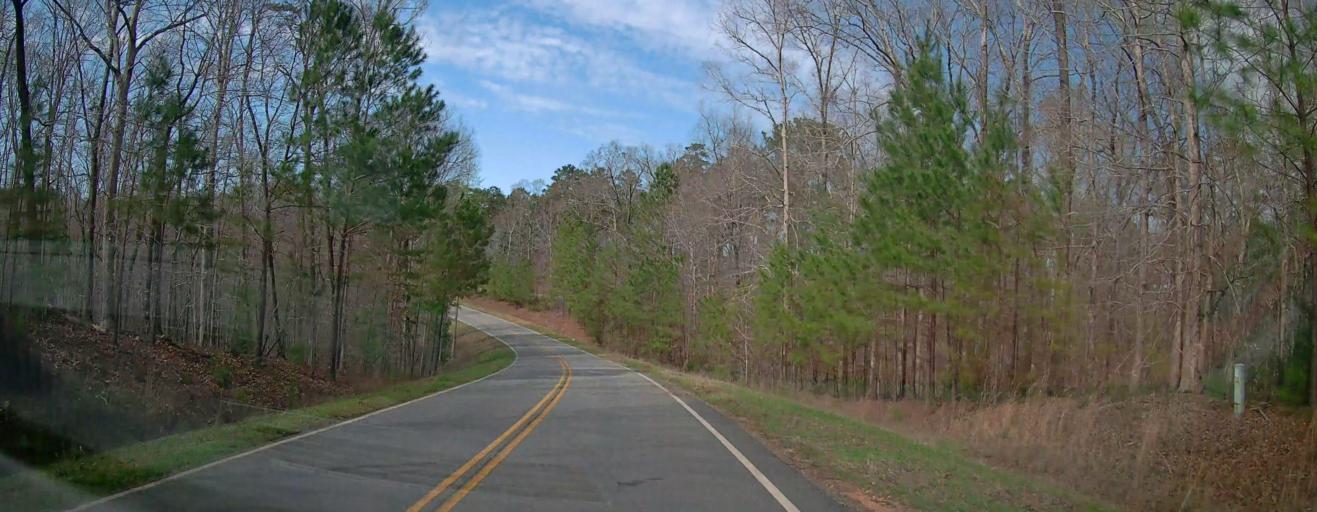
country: US
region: Georgia
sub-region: Monroe County
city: Forsyth
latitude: 33.0881
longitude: -83.7420
